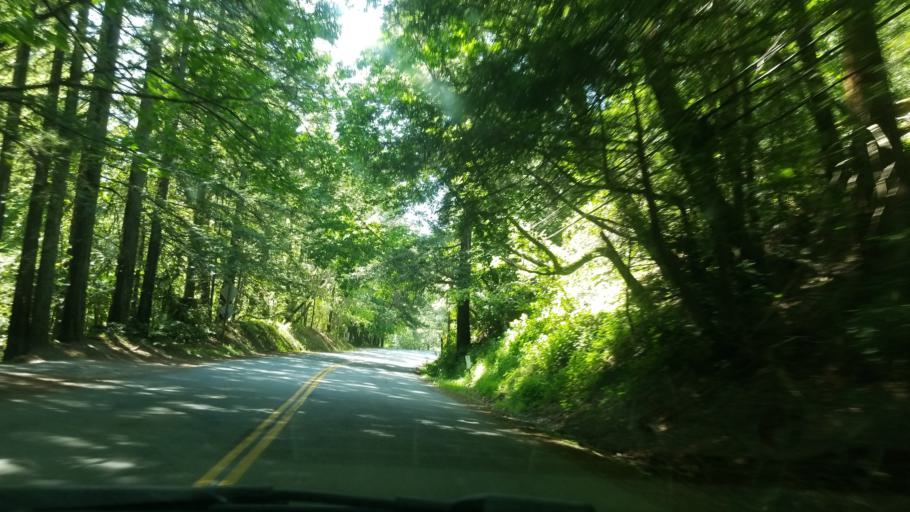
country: US
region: California
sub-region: Santa Clara County
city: Lexington Hills
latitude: 37.1180
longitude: -121.9241
